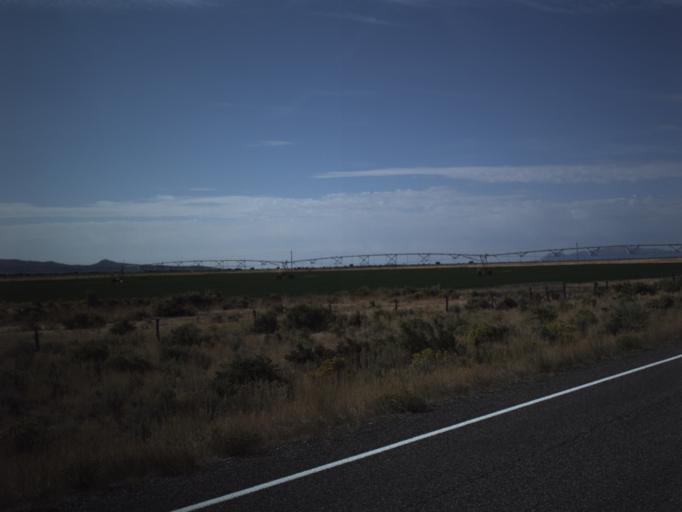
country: US
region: Idaho
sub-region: Cassia County
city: Burley
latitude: 41.7666
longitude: -113.5073
